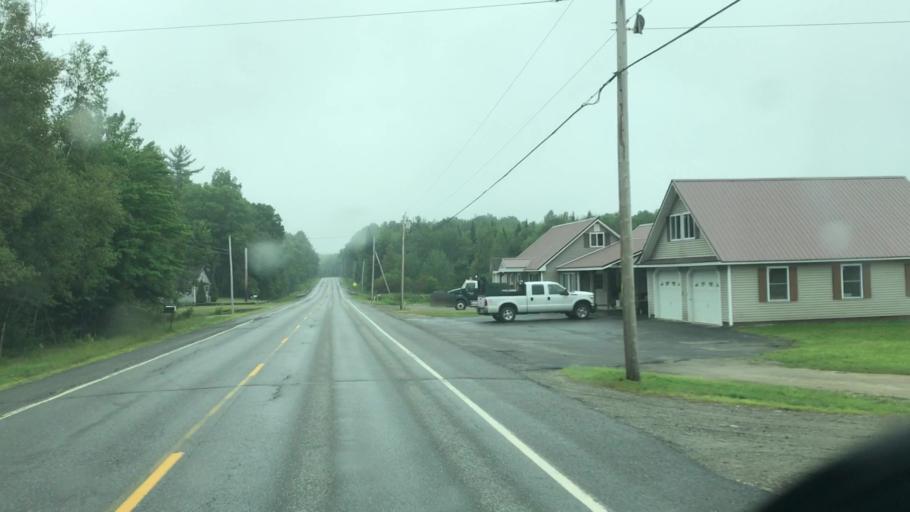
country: US
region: Maine
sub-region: Penobscot County
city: Howland
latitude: 45.2776
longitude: -68.6331
